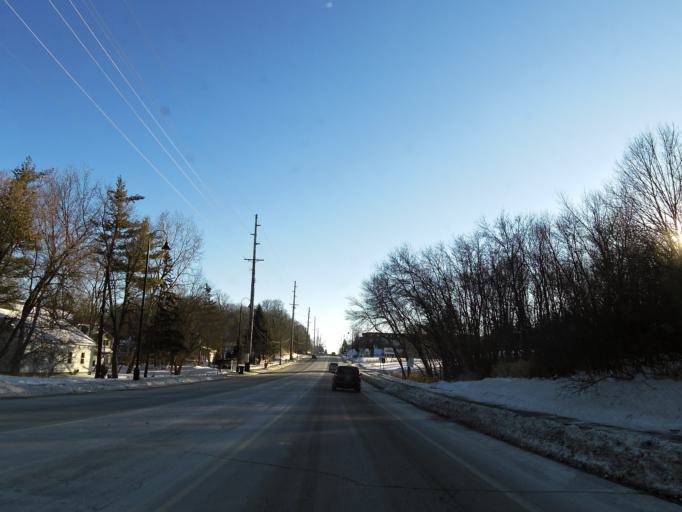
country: US
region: Minnesota
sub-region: Hennepin County
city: Mound
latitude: 44.9469
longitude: -93.6658
